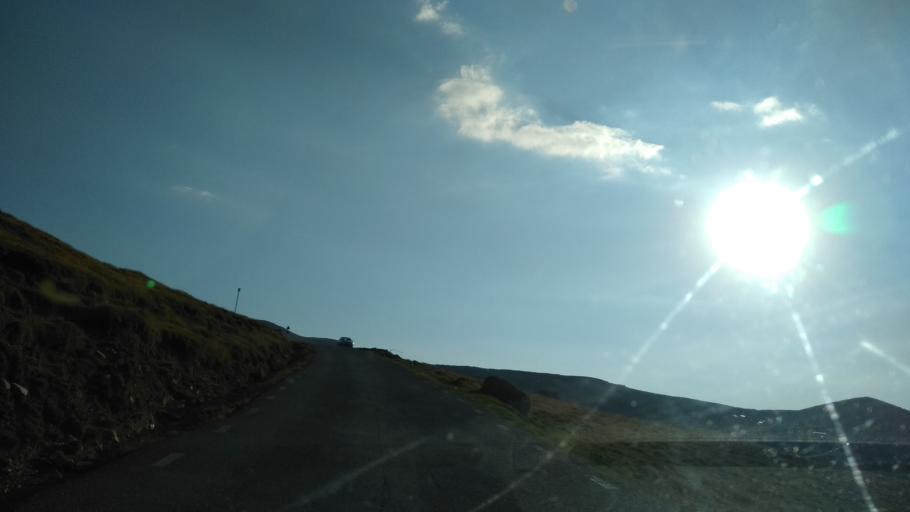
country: RO
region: Prahova
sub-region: Oras Busteni
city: Busteni
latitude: 45.3831
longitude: 25.4738
